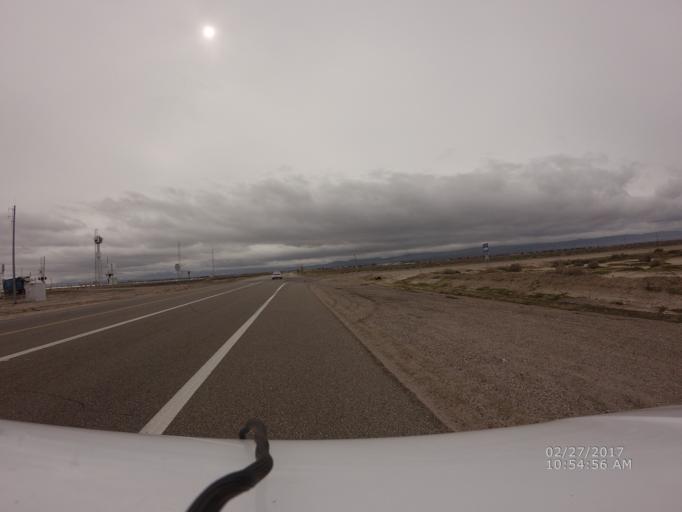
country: US
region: California
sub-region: Los Angeles County
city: Lancaster
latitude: 34.7338
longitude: -118.1423
